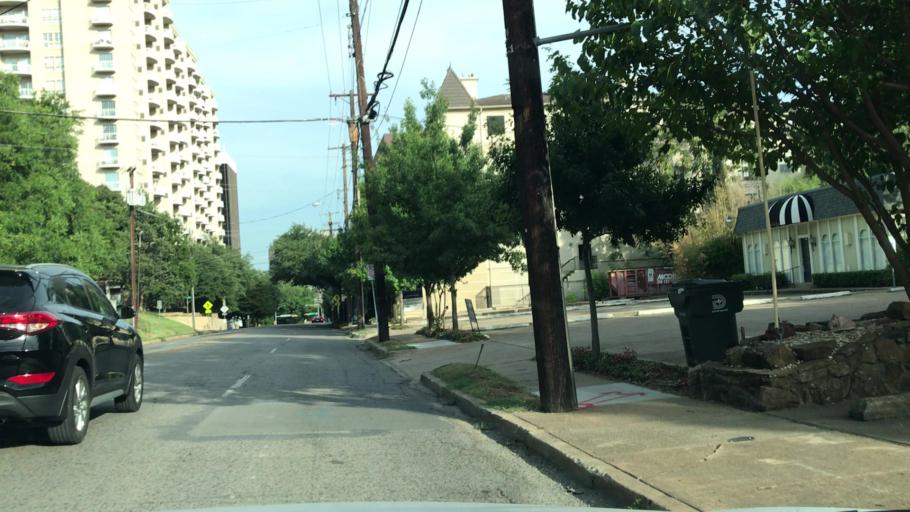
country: US
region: Texas
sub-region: Dallas County
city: Dallas
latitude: 32.8074
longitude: -96.8066
